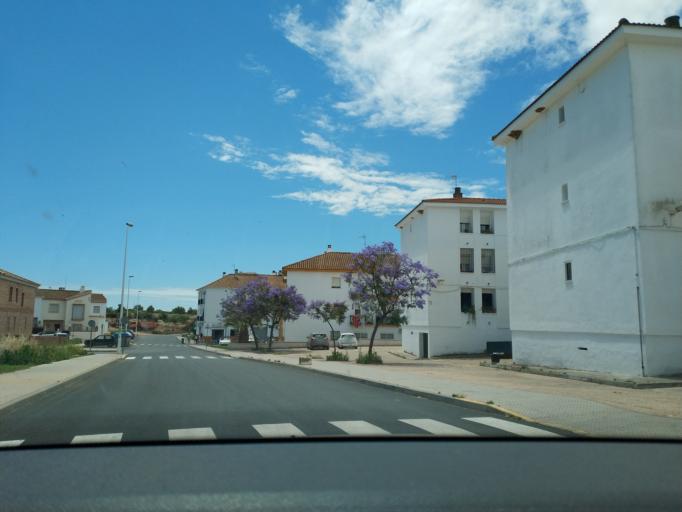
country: ES
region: Andalusia
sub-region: Provincia de Huelva
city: Cartaya
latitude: 37.2844
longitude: -7.1468
